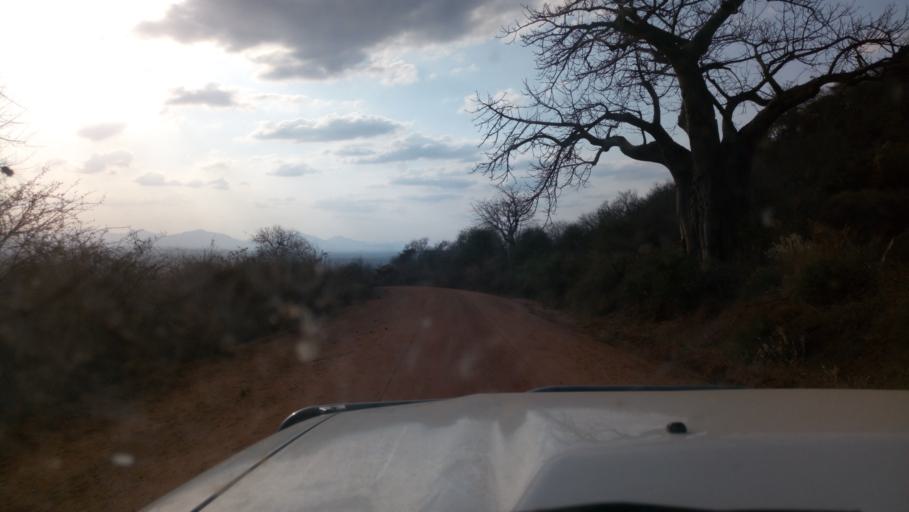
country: KE
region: Kitui
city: Kitui
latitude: -1.6981
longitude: 38.3615
